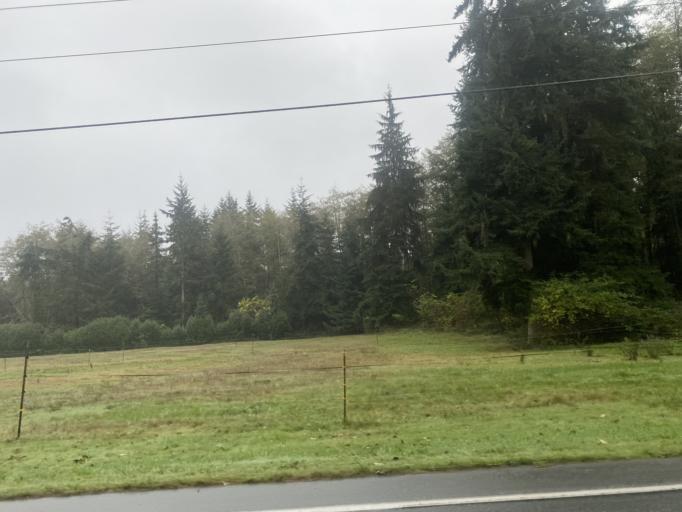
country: US
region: Washington
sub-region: Island County
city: Freeland
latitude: 48.0353
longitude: -122.5070
